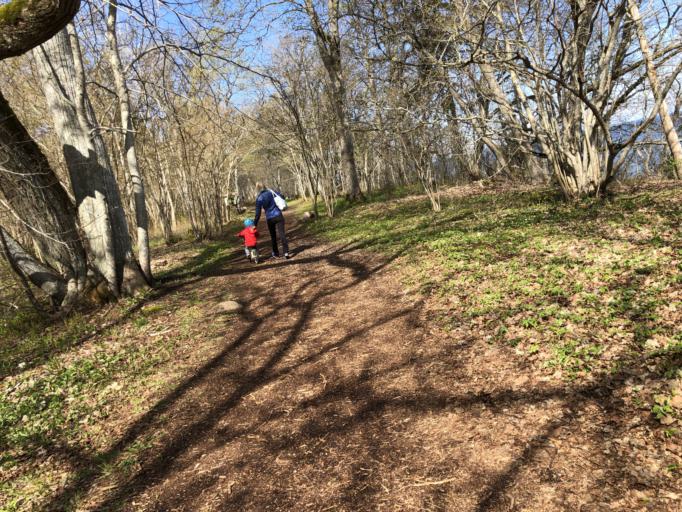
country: EE
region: Harju
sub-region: Harku vald
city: Tabasalu
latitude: 59.4409
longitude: 24.5296
